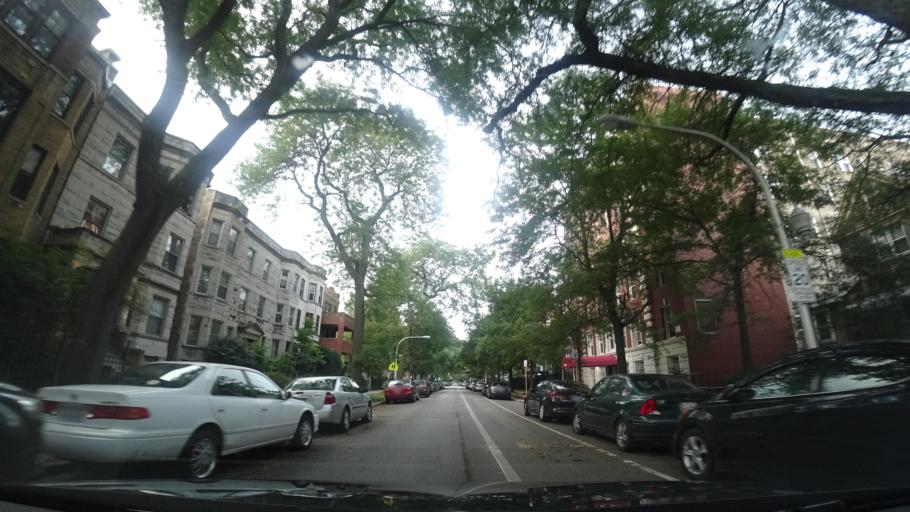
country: US
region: Illinois
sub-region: Cook County
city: Evanston
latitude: 41.9794
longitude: -87.6578
